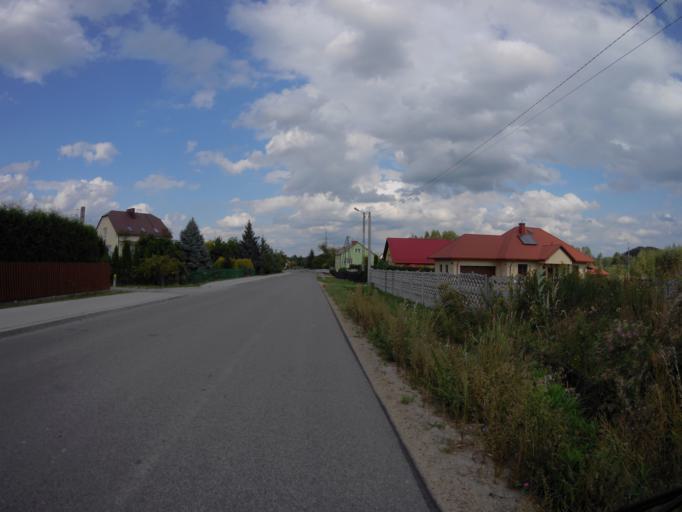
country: PL
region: Subcarpathian Voivodeship
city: Nowa Sarzyna
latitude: 50.2854
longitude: 22.3502
